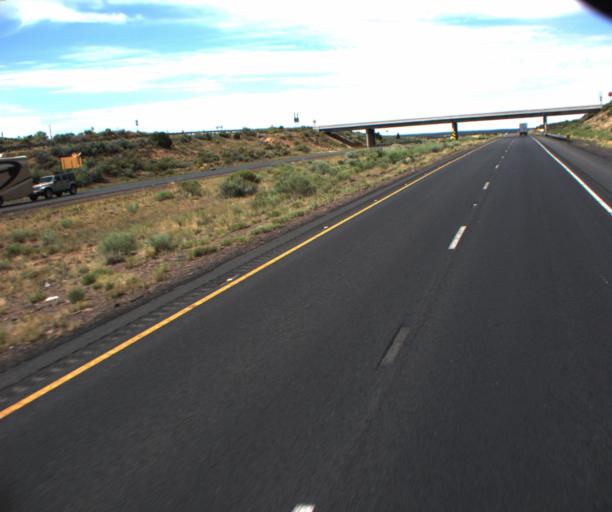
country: US
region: Arizona
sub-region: Apache County
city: Houck
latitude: 35.2894
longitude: -109.1562
